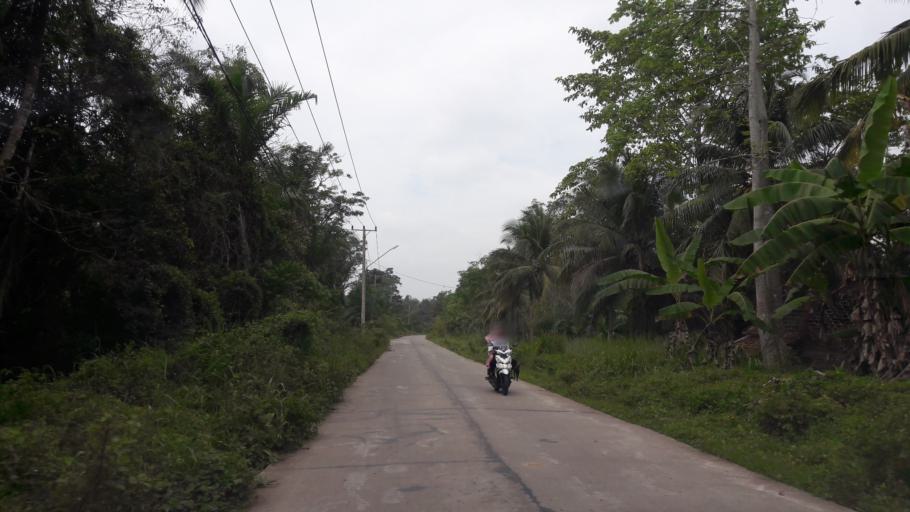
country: ID
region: South Sumatra
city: Gunungmenang
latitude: -3.2273
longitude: 104.1097
